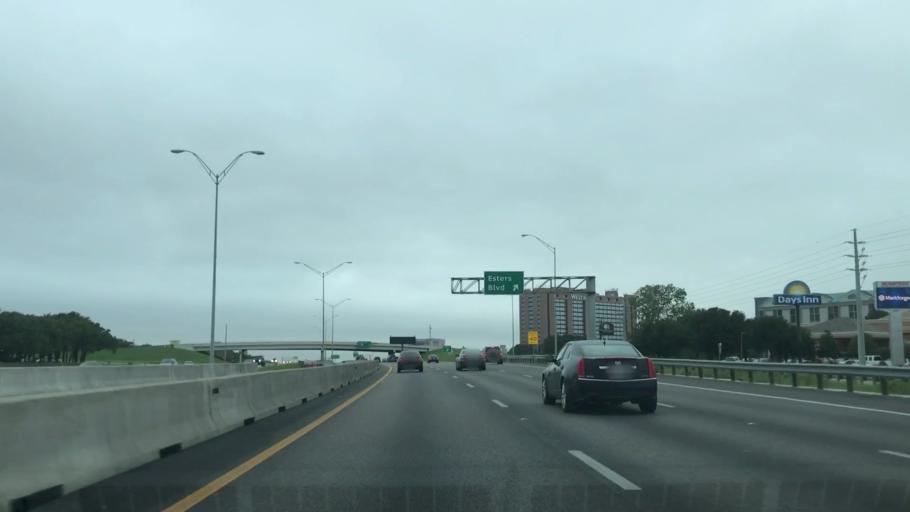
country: US
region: Texas
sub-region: Dallas County
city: Coppell
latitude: 32.9137
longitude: -97.0049
